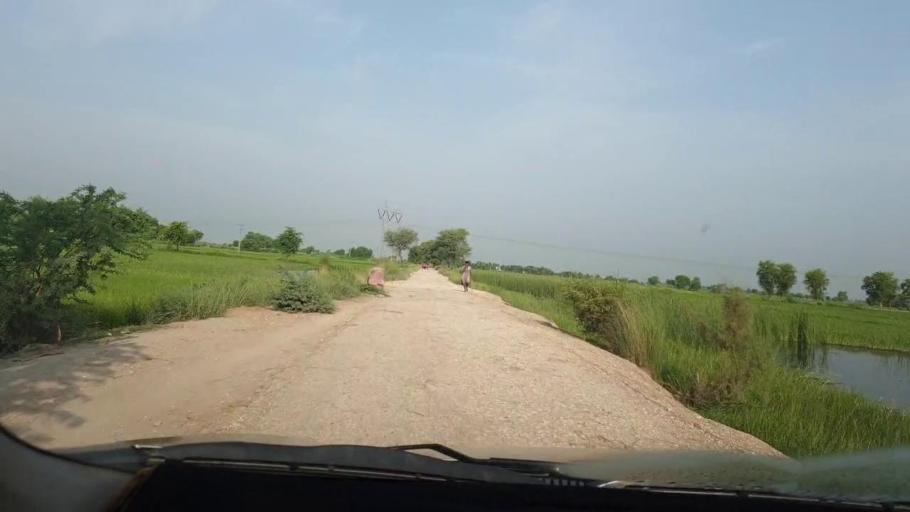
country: PK
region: Sindh
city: Goth Garelo
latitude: 27.4818
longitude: 68.0832
